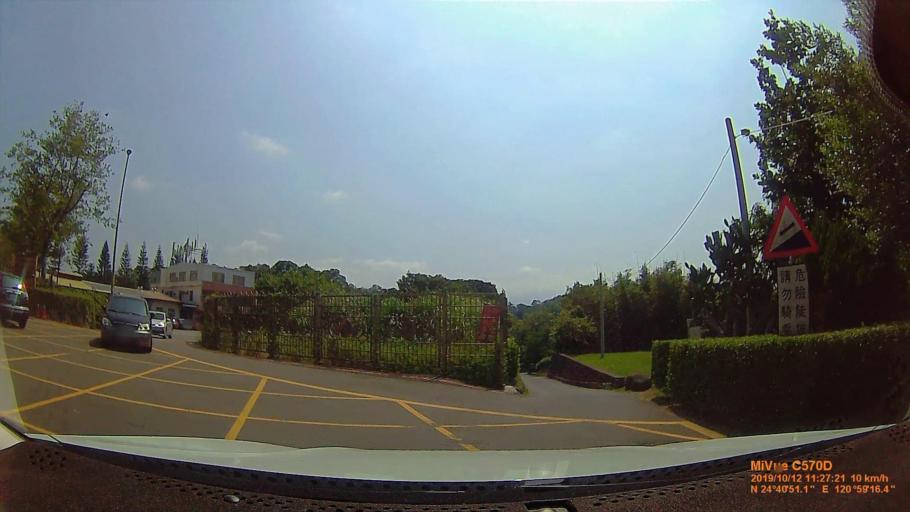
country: TW
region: Taiwan
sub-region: Hsinchu
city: Hsinchu
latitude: 24.6809
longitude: 120.9878
